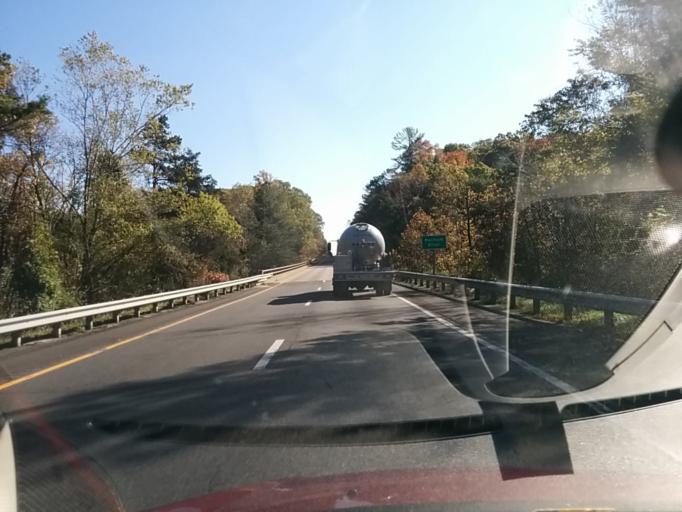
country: US
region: Virginia
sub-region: Albemarle County
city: Crozet
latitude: 38.0301
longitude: -78.6726
